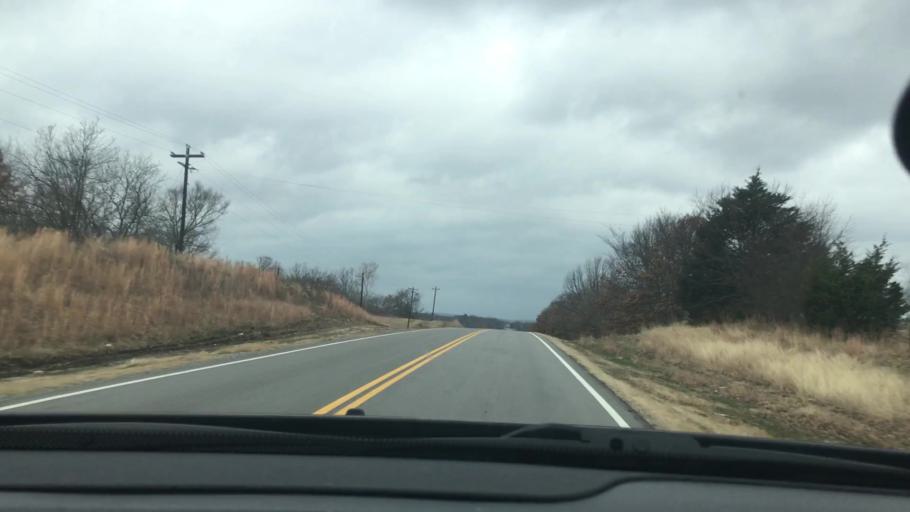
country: US
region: Oklahoma
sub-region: Atoka County
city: Atoka
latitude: 34.3791
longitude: -96.2713
